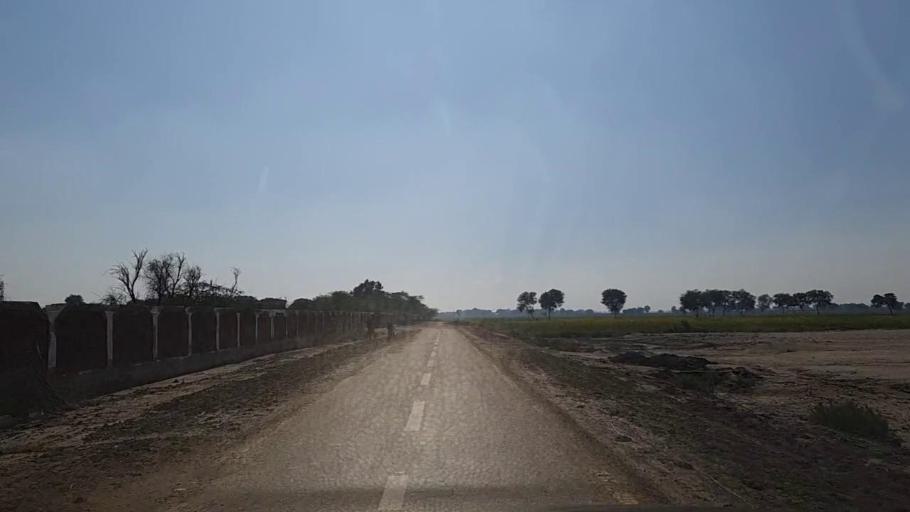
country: PK
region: Sindh
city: Nawabshah
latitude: 26.3197
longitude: 68.3449
